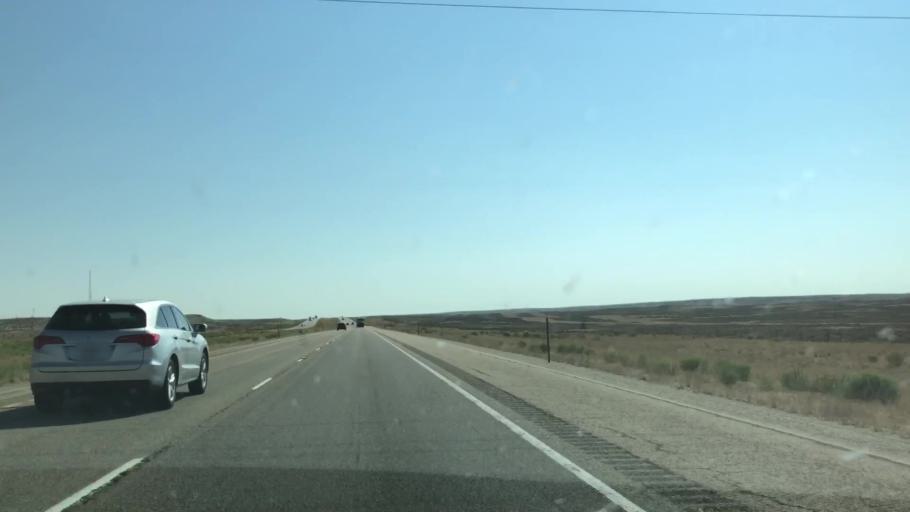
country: US
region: Wyoming
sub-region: Sweetwater County
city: Rock Springs
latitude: 41.6321
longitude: -108.3614
